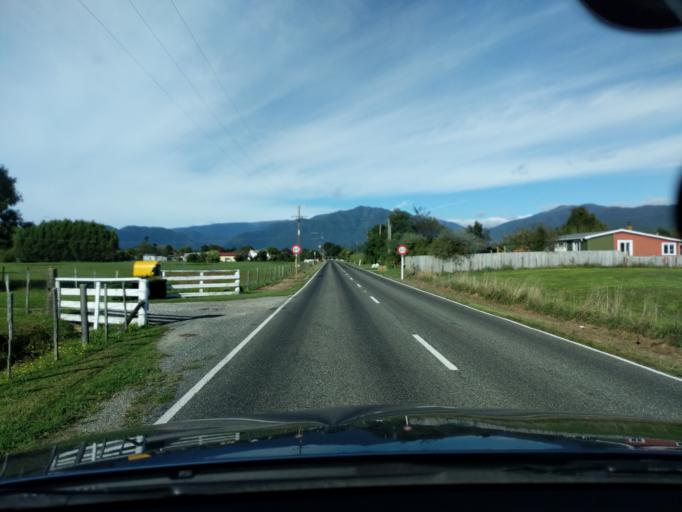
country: NZ
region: Tasman
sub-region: Tasman District
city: Takaka
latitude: -40.8541
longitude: 172.8264
